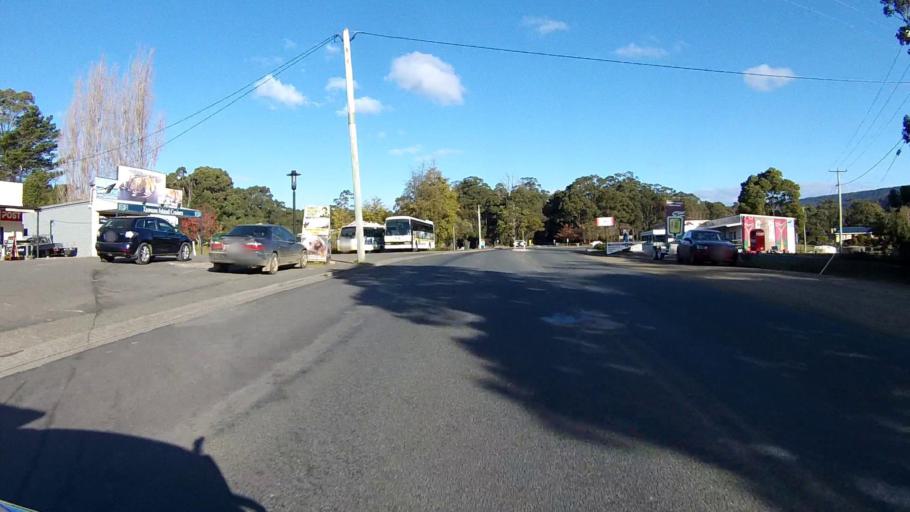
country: AU
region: Tasmania
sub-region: Clarence
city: Sandford
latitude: -43.1395
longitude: 147.8507
